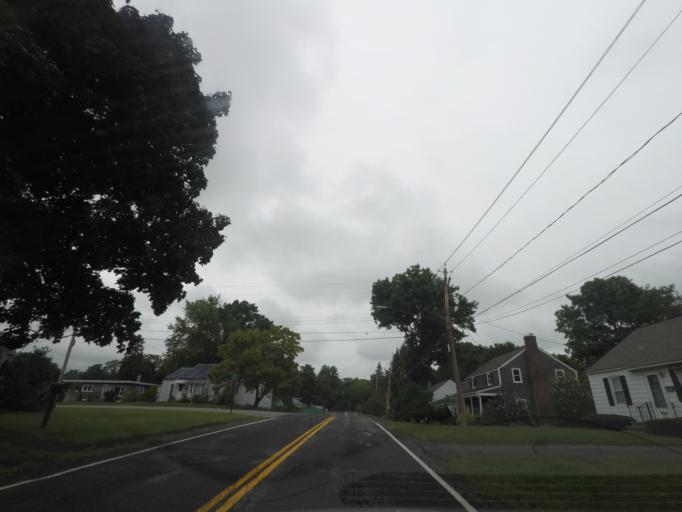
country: US
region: New York
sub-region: Rensselaer County
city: Hampton Manor
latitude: 42.6189
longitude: -73.7179
